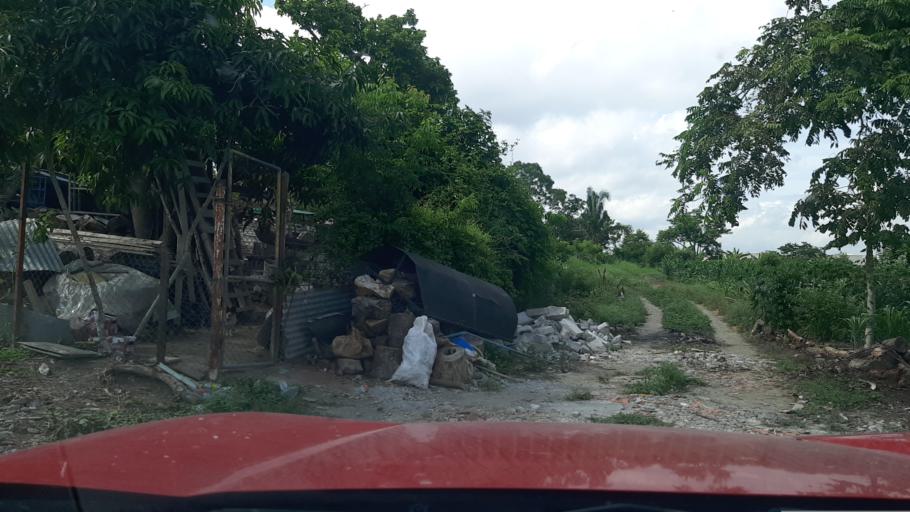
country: MX
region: Veracruz
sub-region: Poza Rica de Hidalgo
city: Villa de las Flores
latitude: 20.5739
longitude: -97.4358
